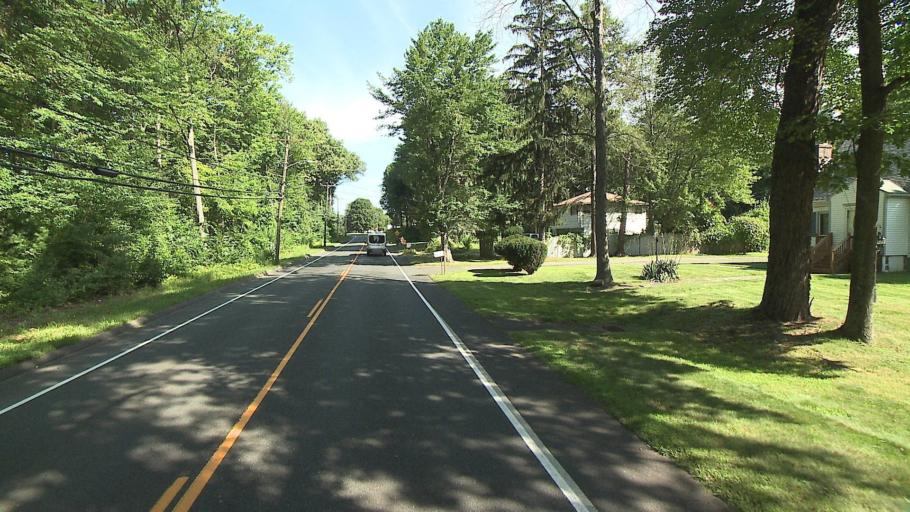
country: US
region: Connecticut
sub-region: Hartford County
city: Blue Hills
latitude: 41.8509
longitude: -72.7020
